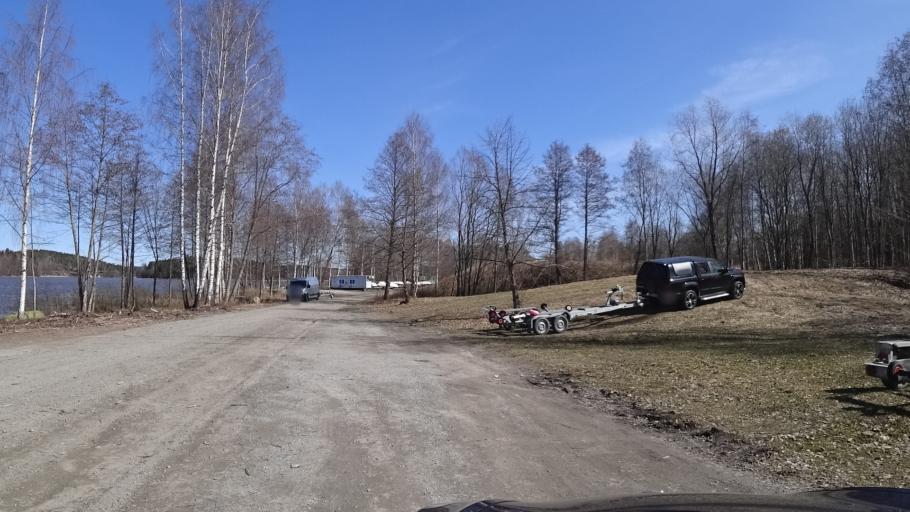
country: FI
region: Uusimaa
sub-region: Helsinki
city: Lohja
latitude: 60.2679
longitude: 24.0615
